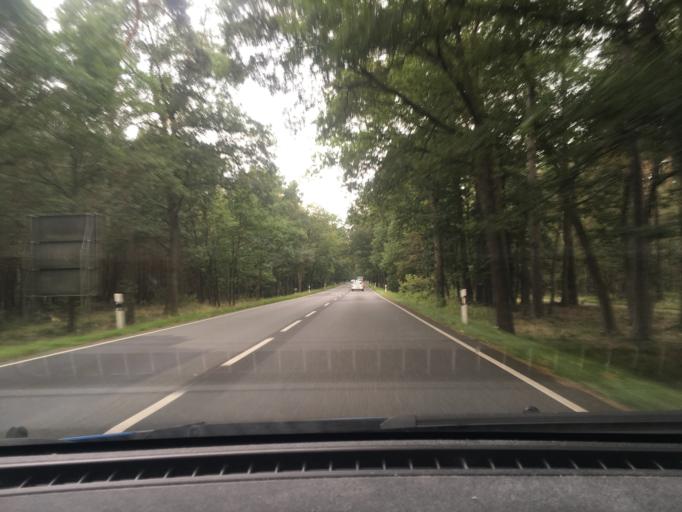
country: DE
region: Lower Saxony
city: Scharnhorst
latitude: 52.7644
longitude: 10.2992
